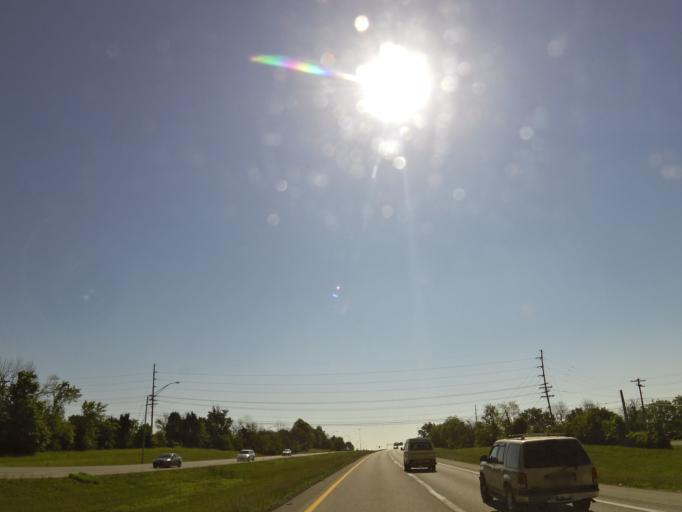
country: US
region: Kentucky
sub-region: Franklin County
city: Frankfort
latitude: 38.1586
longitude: -84.9062
